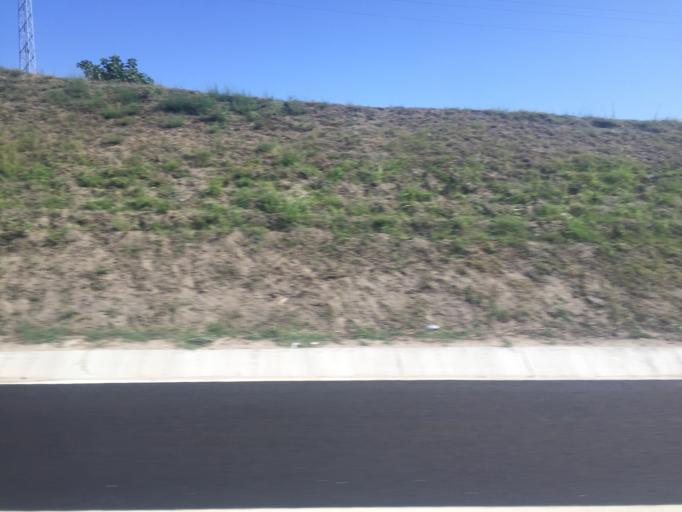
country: TR
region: Bursa
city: Gorukle
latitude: 40.2520
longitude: 28.7462
